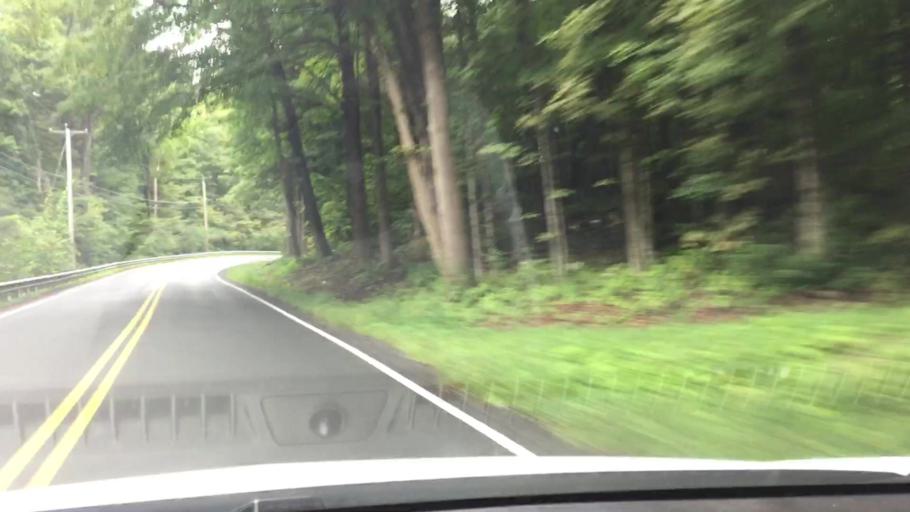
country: US
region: Massachusetts
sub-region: Berkshire County
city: Housatonic
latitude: 42.2989
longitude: -73.3748
